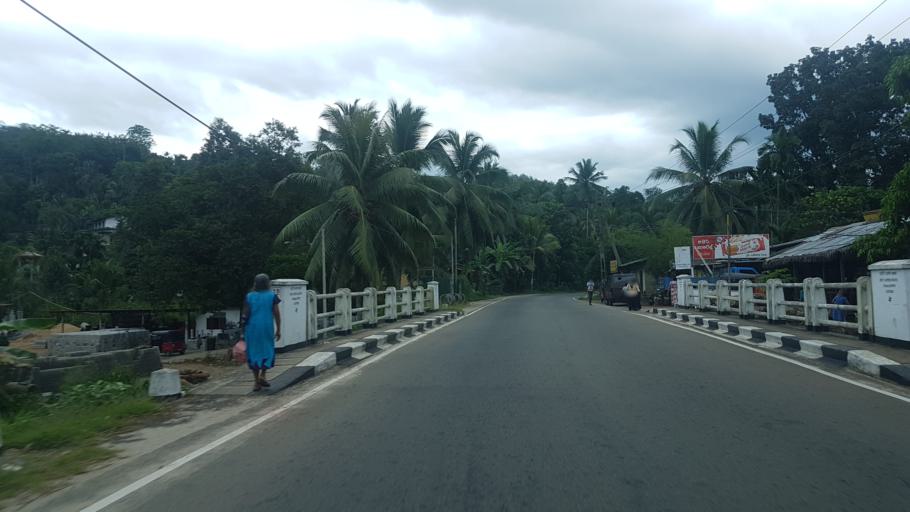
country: LK
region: Western
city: Hanwella Ihala
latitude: 7.0329
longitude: 80.2842
